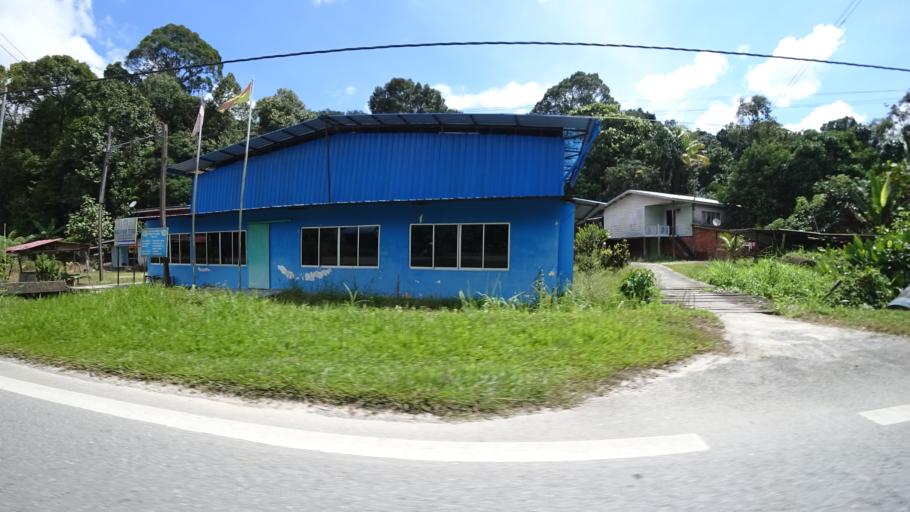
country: MY
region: Sarawak
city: Limbang
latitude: 4.6786
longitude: 114.9813
